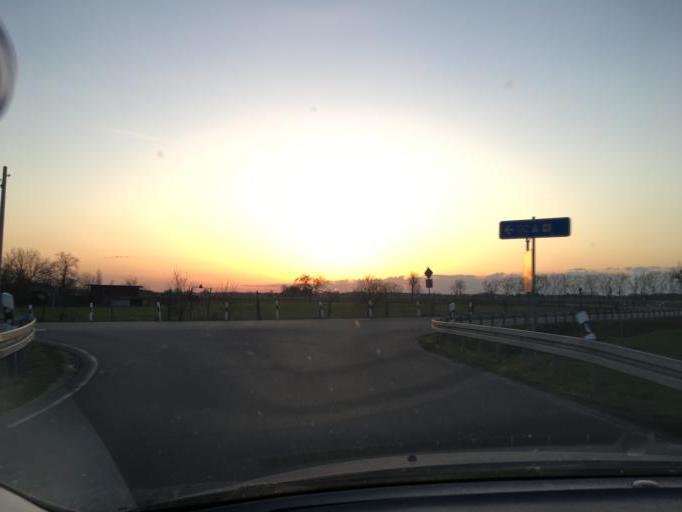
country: DE
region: Saxony
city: Borsdorf
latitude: 51.3270
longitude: 12.5307
